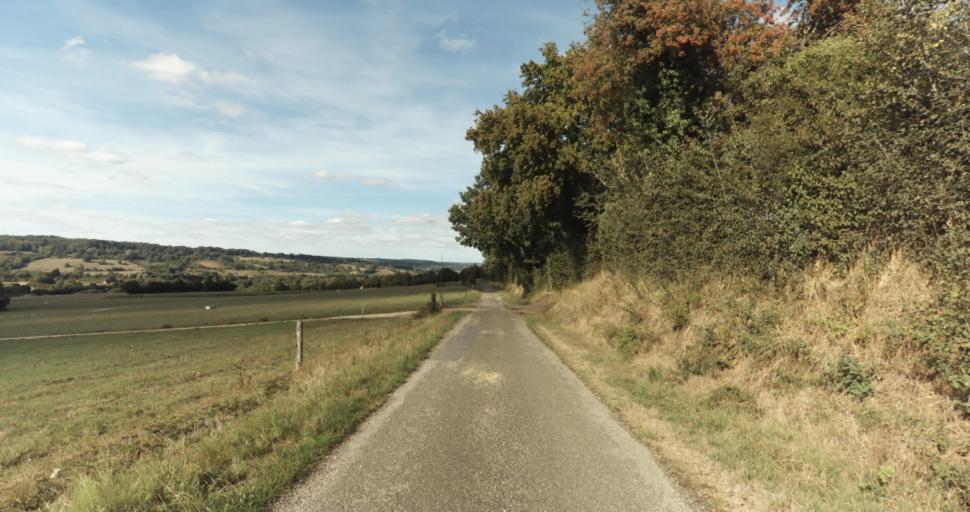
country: FR
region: Lower Normandy
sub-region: Departement de l'Orne
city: Vimoutiers
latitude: 48.9284
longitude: 0.1188
